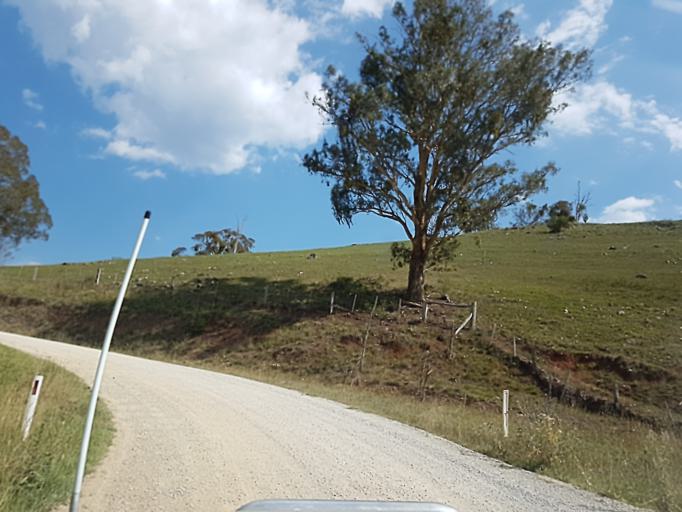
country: AU
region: Victoria
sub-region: East Gippsland
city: Lakes Entrance
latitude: -37.4921
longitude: 148.2263
